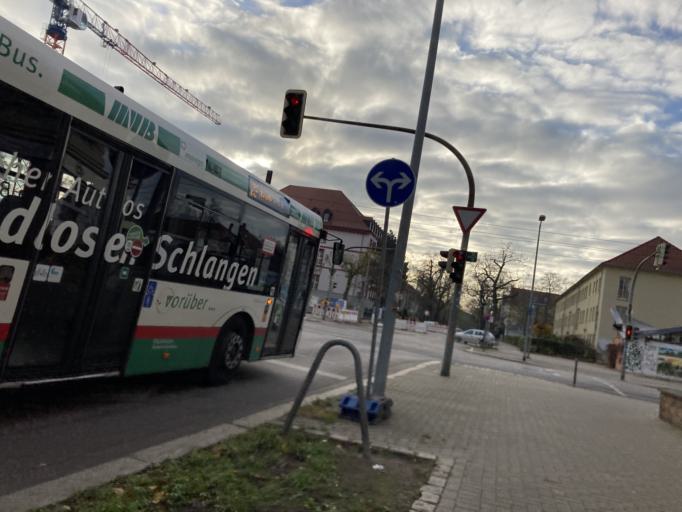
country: DE
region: Saxony-Anhalt
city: Magdeburg
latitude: 52.1307
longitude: 11.6165
